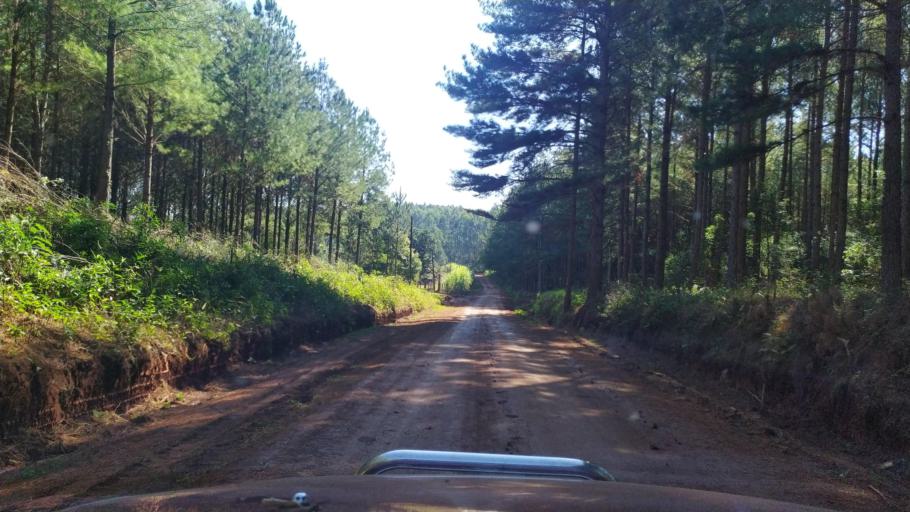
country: AR
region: Misiones
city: El Alcazar
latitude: -26.7262
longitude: -54.6812
